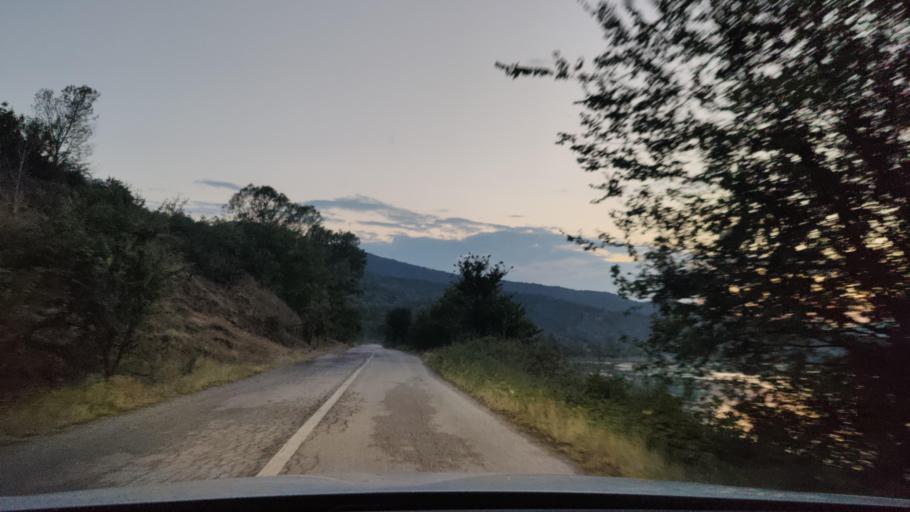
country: GR
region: Central Macedonia
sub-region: Nomos Serron
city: Chrysochorafa
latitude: 41.1977
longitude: 23.0898
